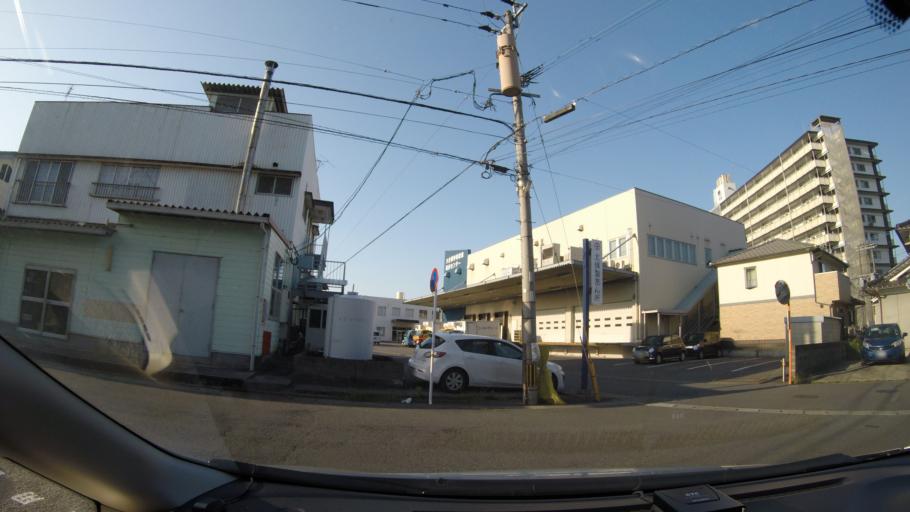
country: JP
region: Oita
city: Oita
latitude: 33.2113
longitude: 131.6097
